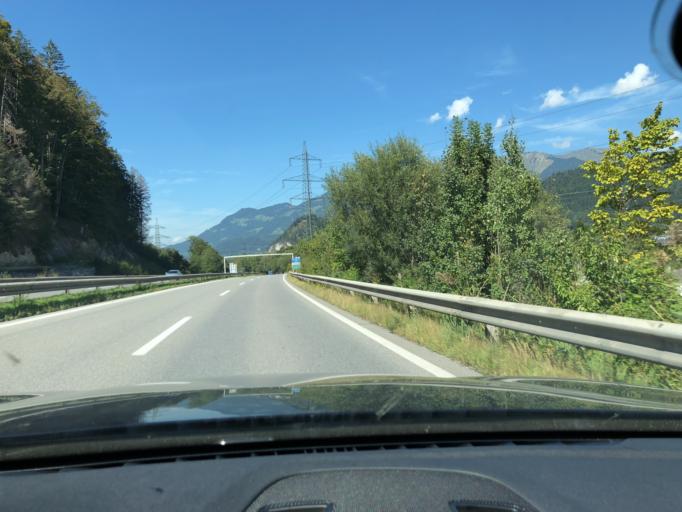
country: AT
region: Vorarlberg
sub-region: Politischer Bezirk Bludenz
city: Nuziders
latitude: 47.1611
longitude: 9.7975
